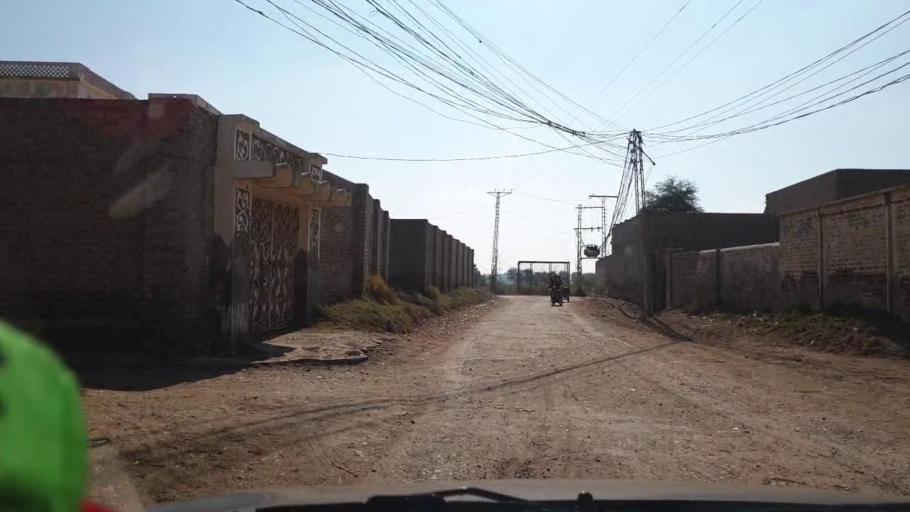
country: PK
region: Sindh
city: Sinjhoro
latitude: 25.9478
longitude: 68.7459
